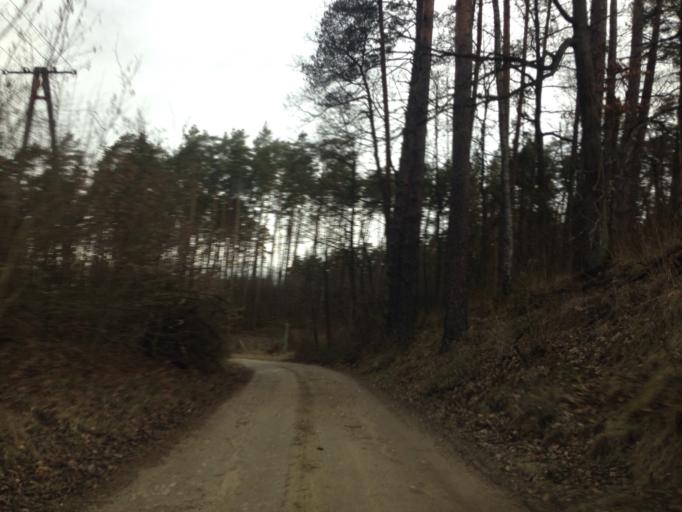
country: PL
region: Kujawsko-Pomorskie
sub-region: Powiat brodnicki
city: Gorzno
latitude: 53.1786
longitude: 19.6793
